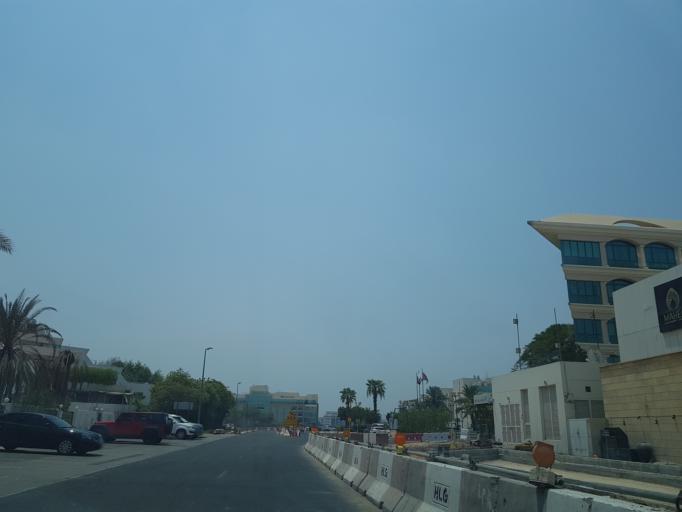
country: AE
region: Ash Shariqah
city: Sharjah
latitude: 25.2469
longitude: 55.3462
